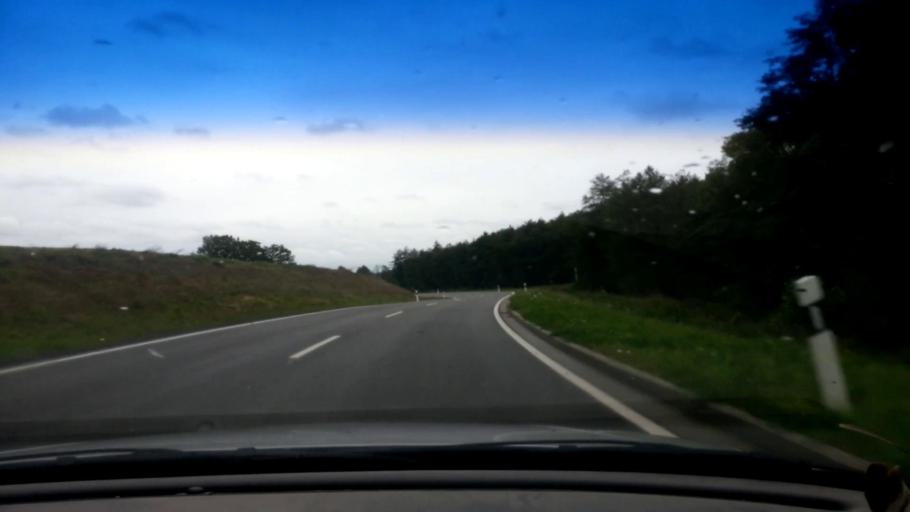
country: DE
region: Bavaria
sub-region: Regierungsbezirk Unterfranken
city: Stettfeld
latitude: 50.0059
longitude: 10.7406
